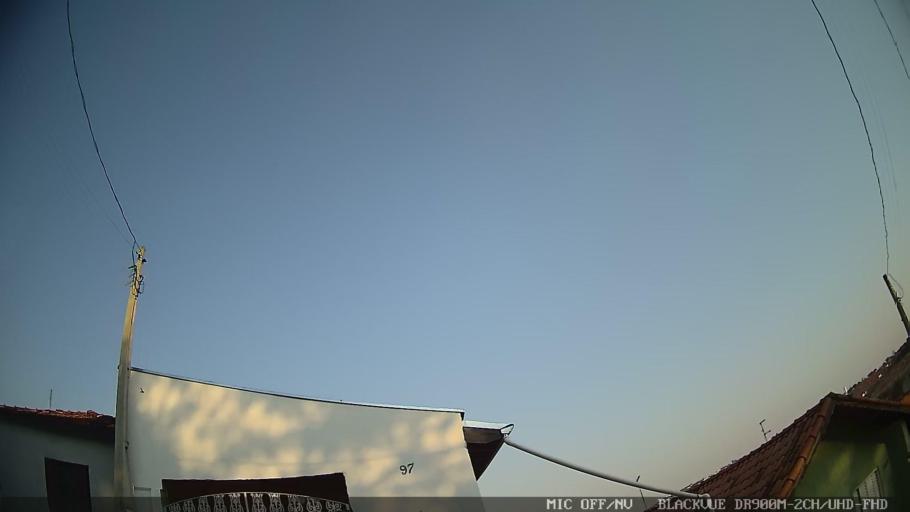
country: BR
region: Sao Paulo
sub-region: Itatiba
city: Itatiba
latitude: -23.0103
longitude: -46.8296
